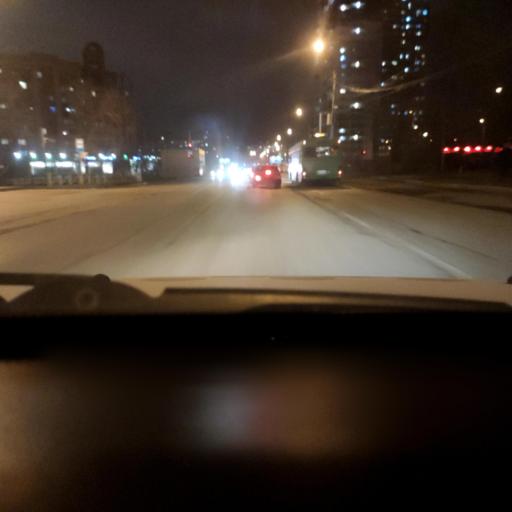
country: RU
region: Perm
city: Perm
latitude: 57.9693
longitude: 56.2271
